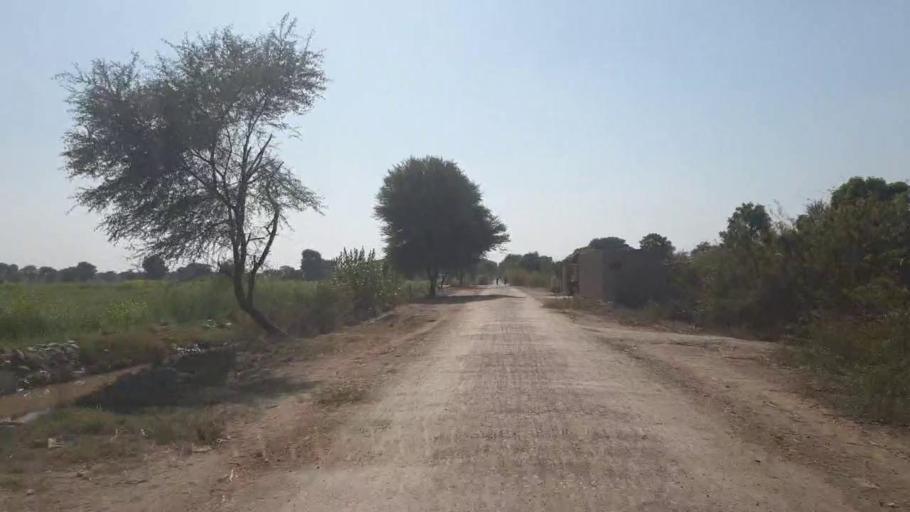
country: PK
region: Sindh
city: Chambar
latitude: 25.2940
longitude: 68.6876
